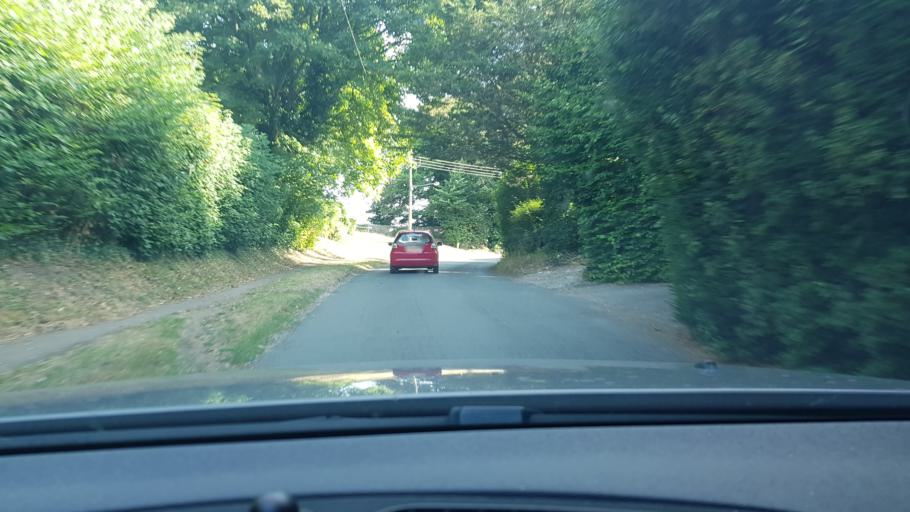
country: GB
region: England
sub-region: Wiltshire
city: Ramsbury
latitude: 51.4460
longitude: -1.6005
